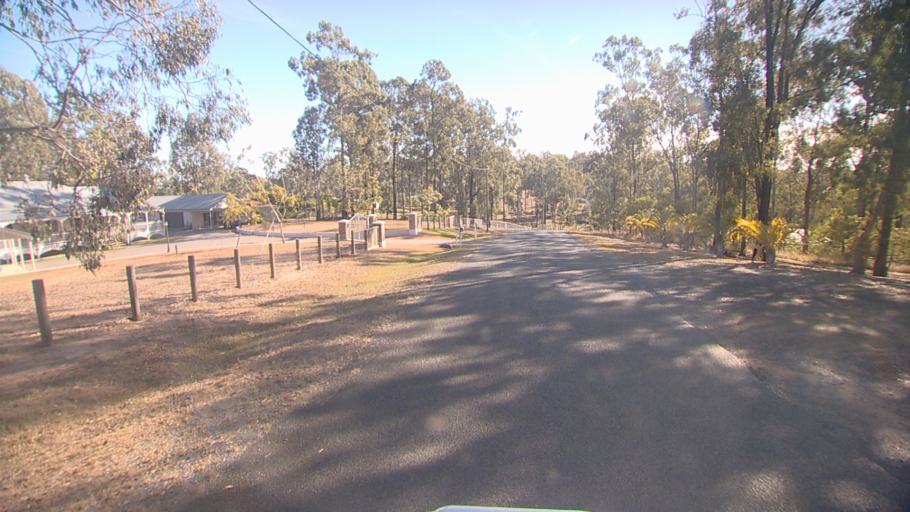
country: AU
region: Queensland
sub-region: Ipswich
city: Springfield Lakes
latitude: -27.7018
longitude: 152.9264
